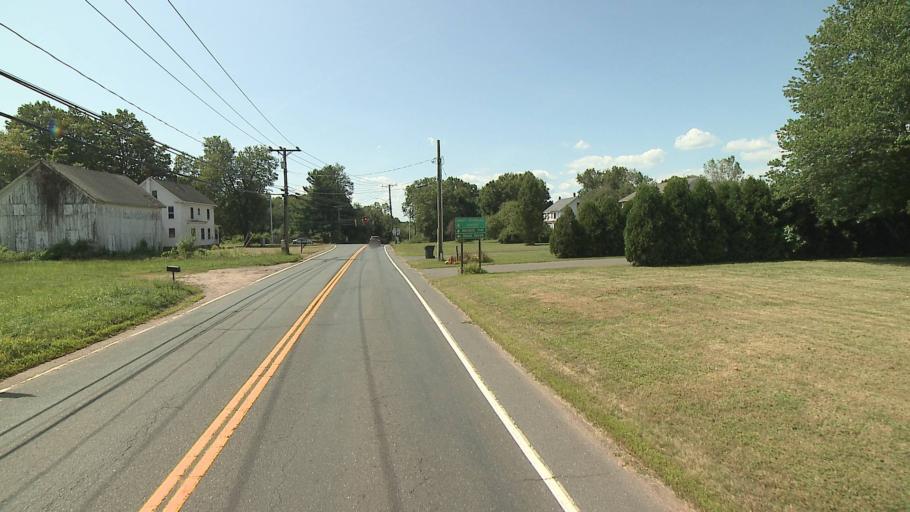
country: US
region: Connecticut
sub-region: Hartford County
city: Broad Brook
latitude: 41.9260
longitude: -72.5431
